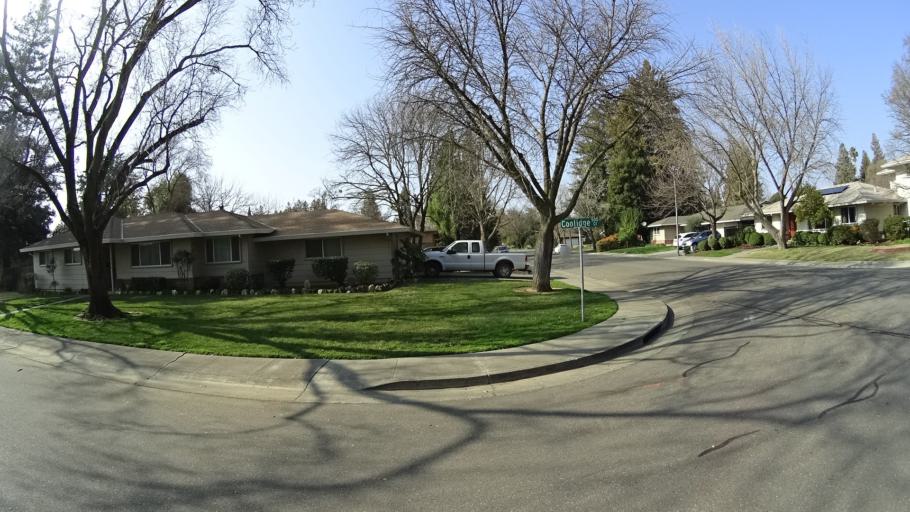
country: US
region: California
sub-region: Yolo County
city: Davis
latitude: 38.5474
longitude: -121.7739
